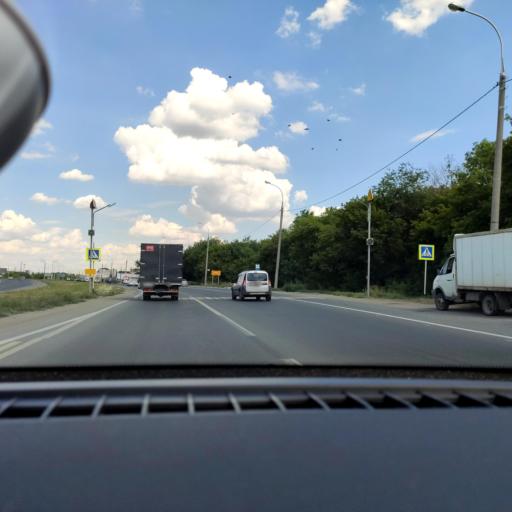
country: RU
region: Samara
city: Smyshlyayevka
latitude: 53.2557
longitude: 50.3726
